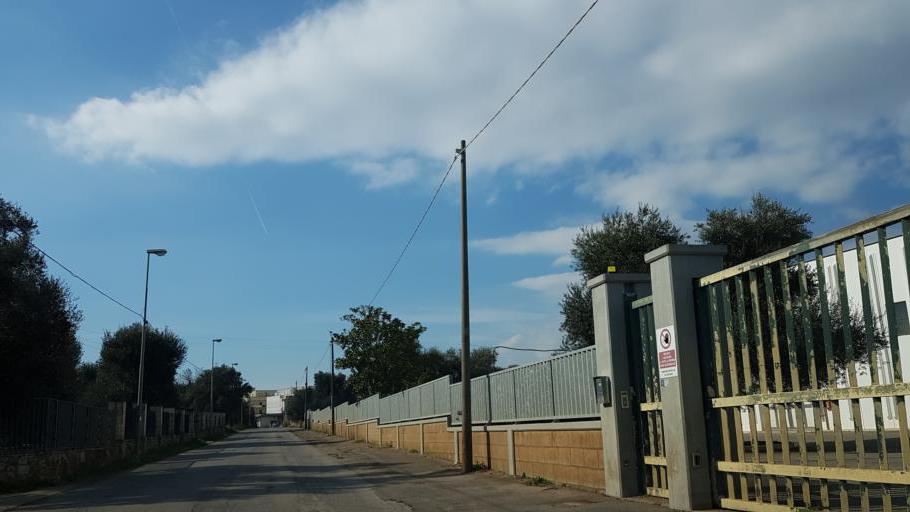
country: IT
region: Apulia
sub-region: Provincia di Brindisi
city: Carovigno
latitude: 40.7116
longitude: 17.6676
